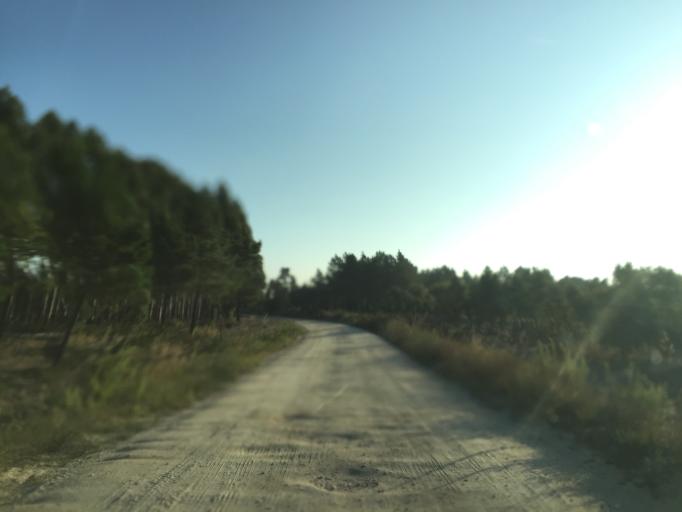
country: PT
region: Portalegre
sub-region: Ponte de Sor
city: Santo Andre
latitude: 39.1282
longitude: -8.3206
